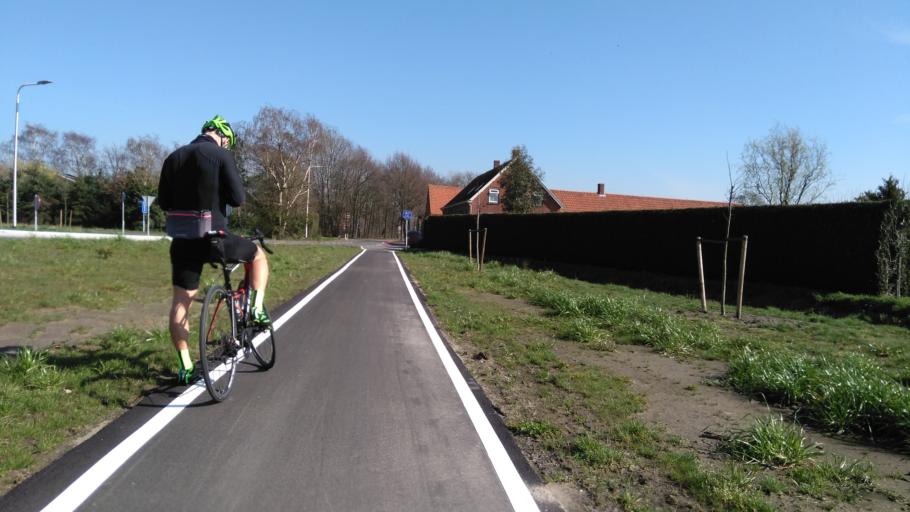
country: NL
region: North Brabant
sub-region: Gemeente Baarle-Nassau
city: Baarle-Nassau
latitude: 51.4396
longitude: 4.9463
